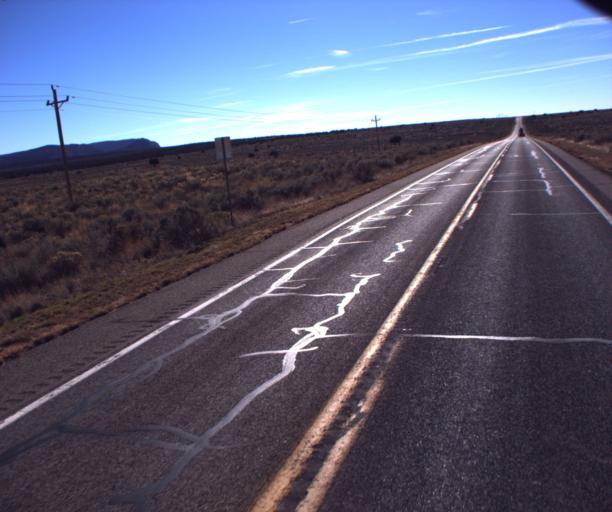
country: US
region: Arizona
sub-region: Mohave County
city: Colorado City
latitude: 36.9142
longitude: -112.9303
